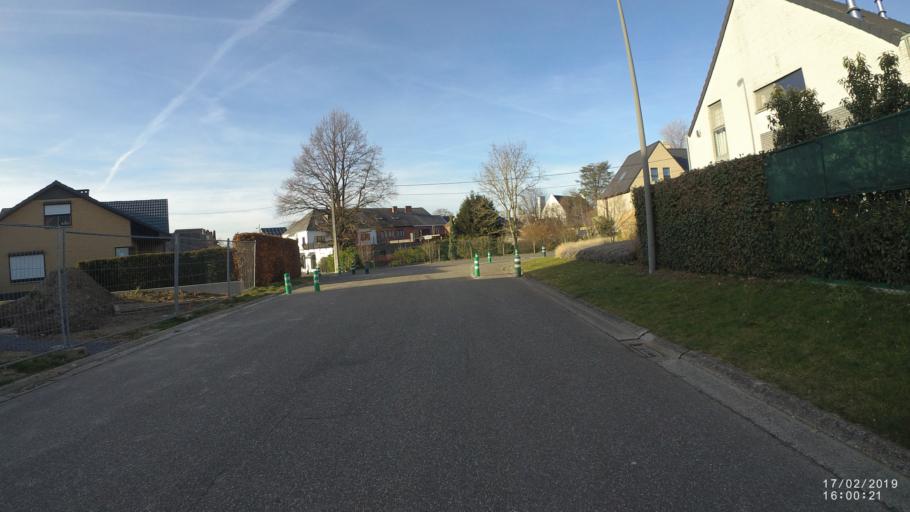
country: BE
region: Flanders
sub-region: Provincie Limburg
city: Alken
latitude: 50.8990
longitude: 5.3098
